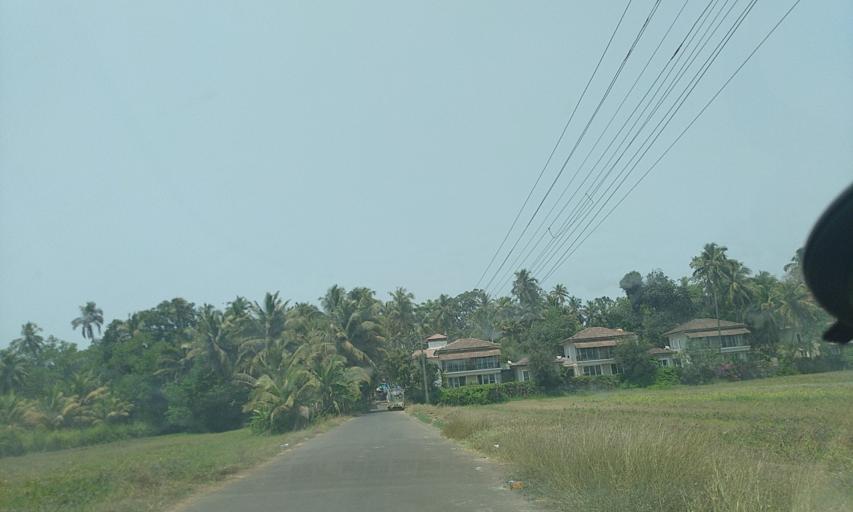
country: IN
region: Goa
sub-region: North Goa
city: Saligao
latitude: 15.5481
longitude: 73.7861
